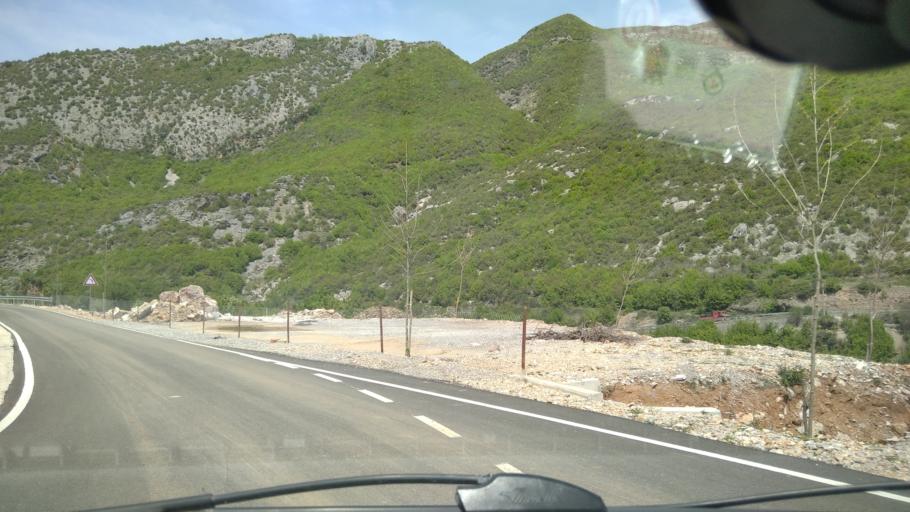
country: AL
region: Shkoder
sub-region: Rrethi i Shkodres
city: Guri i Zi
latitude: 42.1290
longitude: 19.6139
